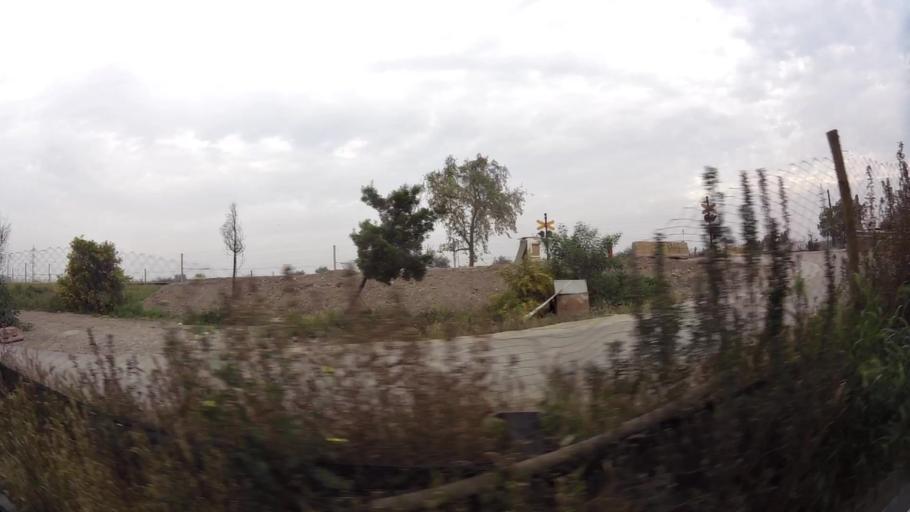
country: CL
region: Santiago Metropolitan
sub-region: Provincia de Santiago
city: Lo Prado
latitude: -33.4817
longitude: -70.7032
